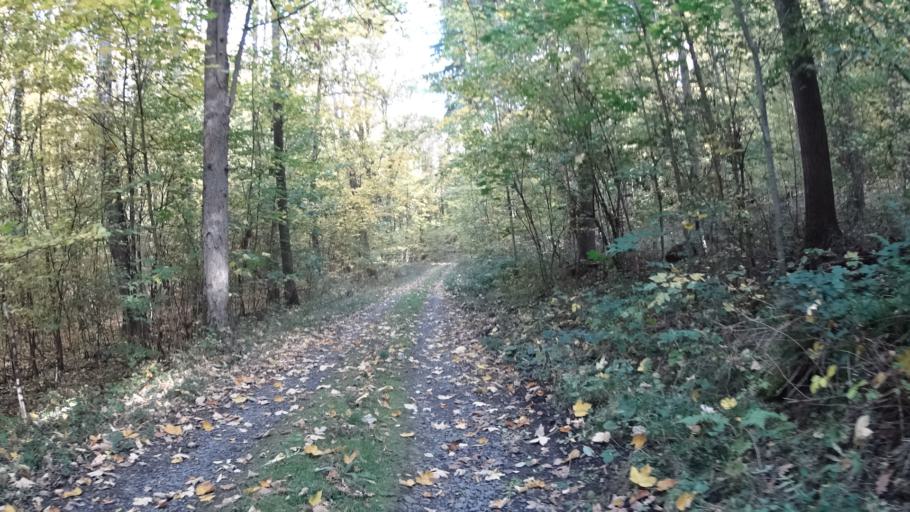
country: DE
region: Rheinland-Pfalz
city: Stein-Bockenheim
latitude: 49.7503
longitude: 7.9630
